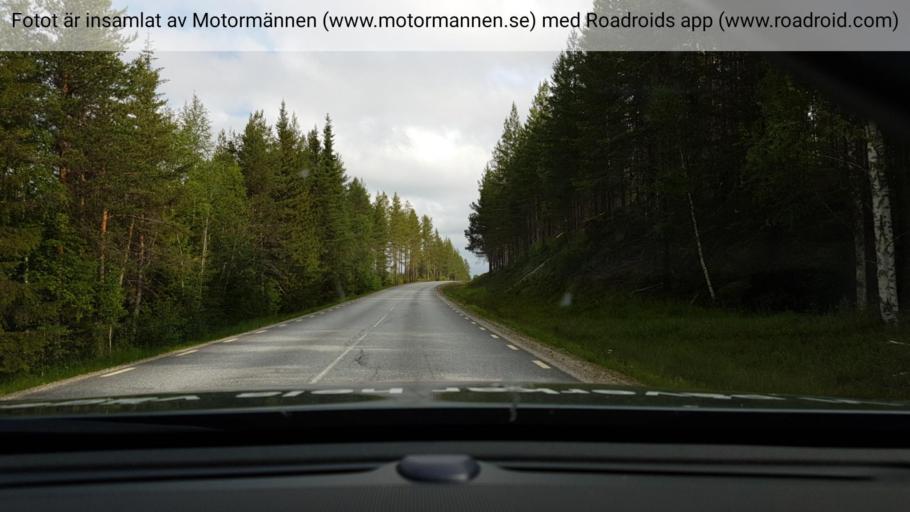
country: SE
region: Vaesterbotten
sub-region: Vindelns Kommun
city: Vindeln
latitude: 64.3915
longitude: 19.3755
